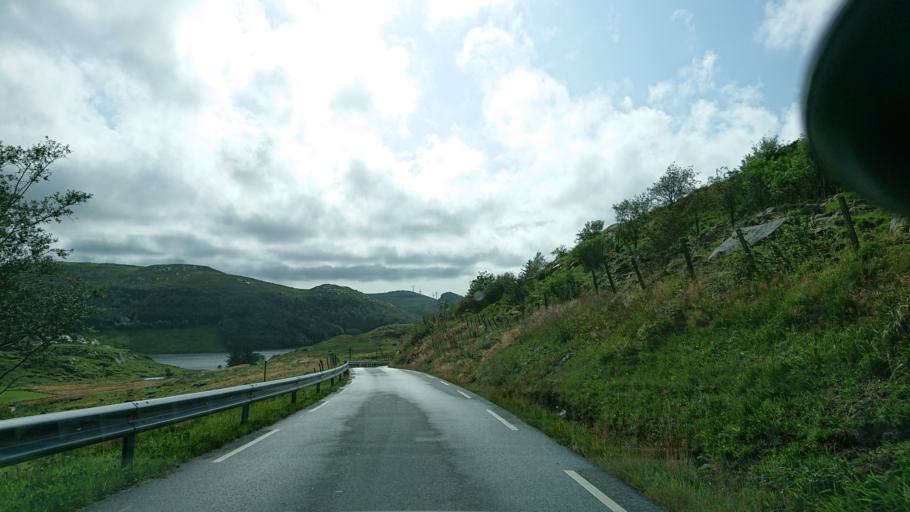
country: NO
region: Rogaland
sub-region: Gjesdal
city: Algard
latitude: 58.6790
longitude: 5.8488
